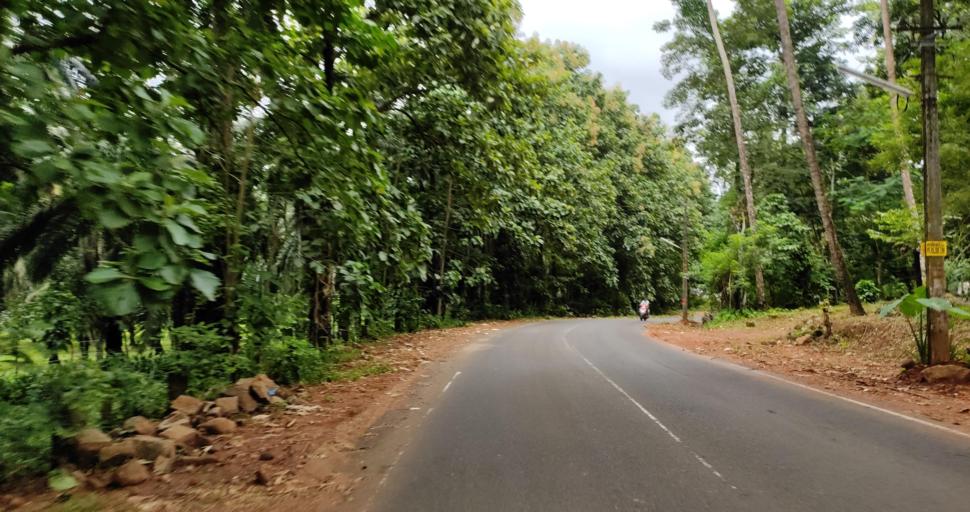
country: IN
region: Kerala
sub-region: Ernakulam
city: Angamali
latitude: 10.2912
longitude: 76.5003
